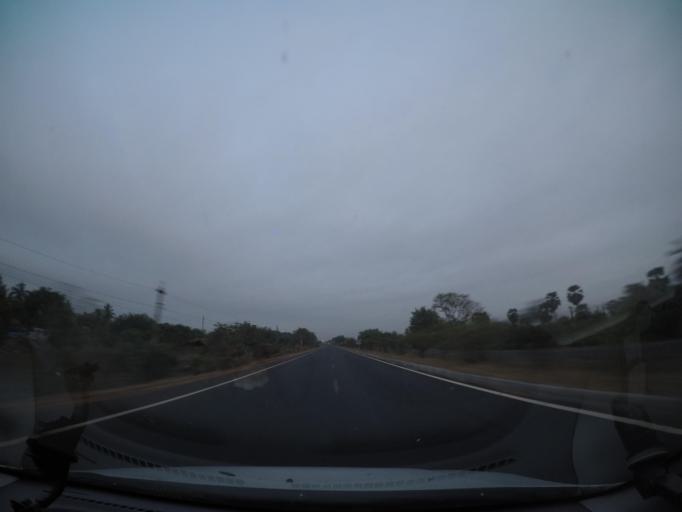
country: IN
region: Andhra Pradesh
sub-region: West Godavari
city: Tadepallegudem
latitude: 16.8094
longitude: 81.3292
